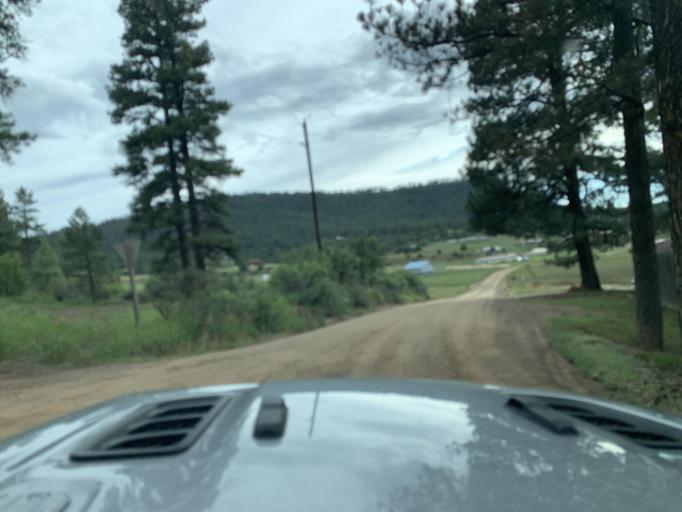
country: US
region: Colorado
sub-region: Archuleta County
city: Pagosa Springs
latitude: 37.2217
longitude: -107.1839
